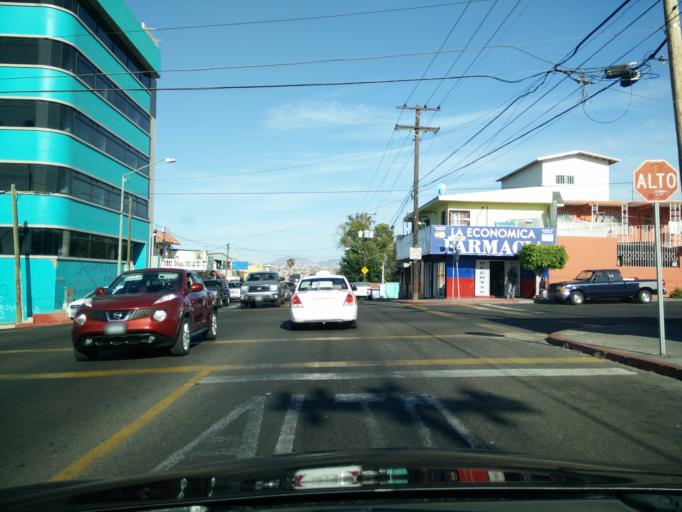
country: MX
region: Baja California
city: Tijuana
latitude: 32.5266
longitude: -117.0454
